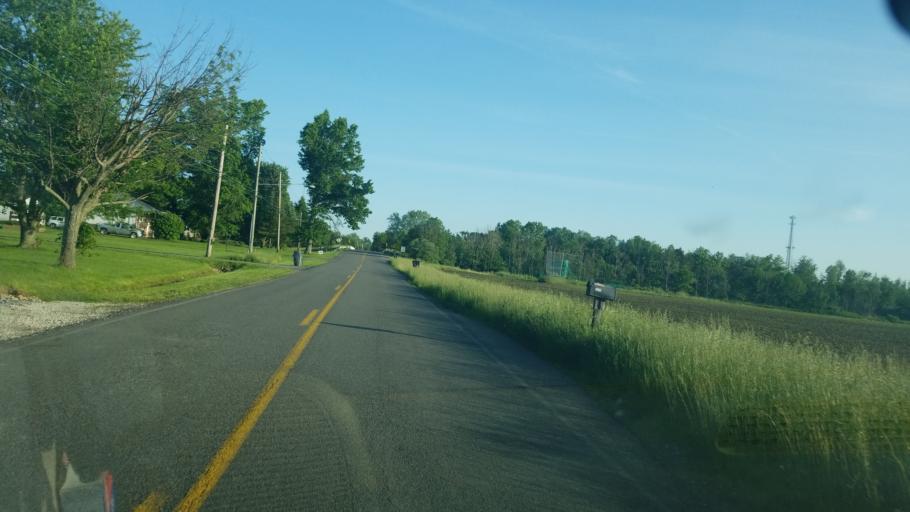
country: US
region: Ohio
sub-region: Portage County
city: Ravenna
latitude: 41.1080
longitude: -81.1460
